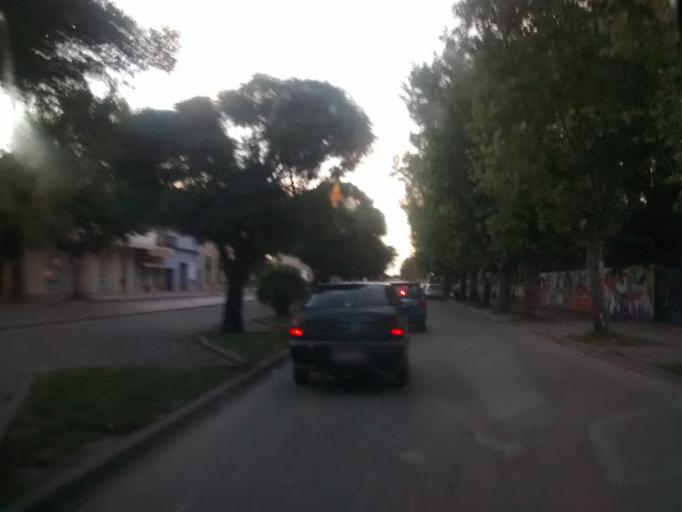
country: AR
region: Buenos Aires
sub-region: Partido de Loberia
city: Loberia
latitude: -38.1648
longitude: -58.7813
